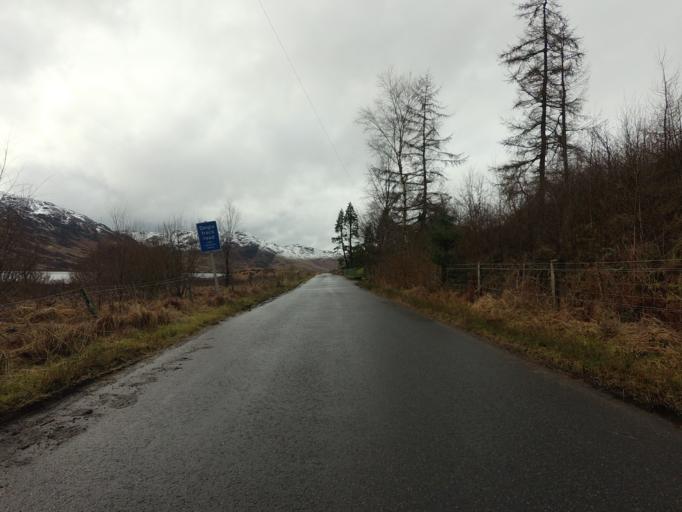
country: GB
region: Scotland
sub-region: West Dunbartonshire
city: Balloch
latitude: 56.2539
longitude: -4.5901
